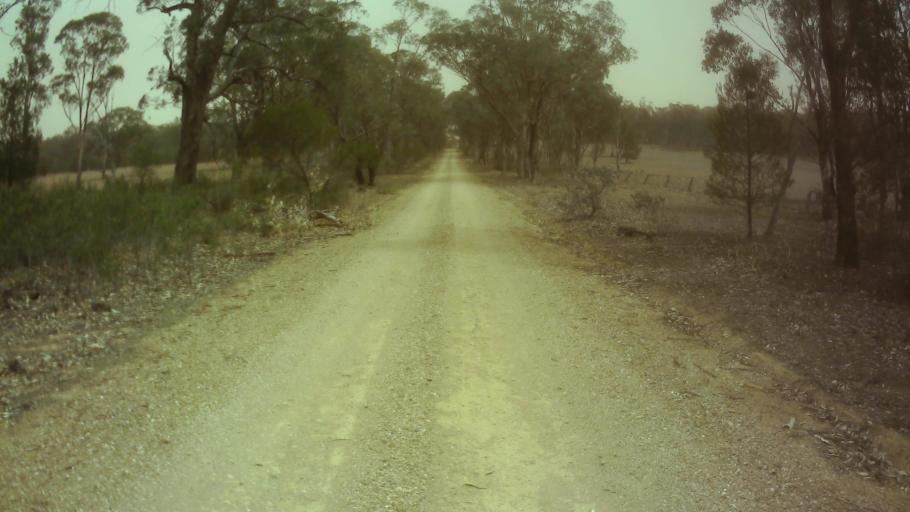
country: AU
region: New South Wales
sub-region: Weddin
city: Grenfell
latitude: -33.7099
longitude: 147.9522
